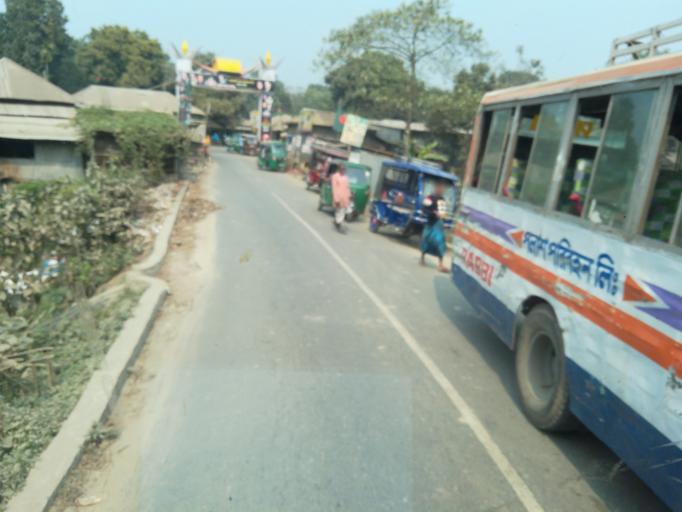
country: BD
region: Dhaka
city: Nagarpur
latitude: 23.9963
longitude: 89.8461
